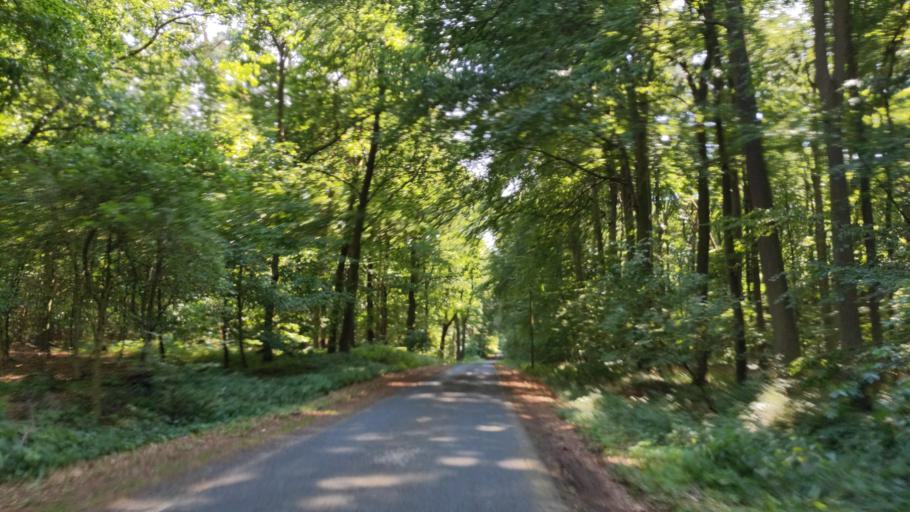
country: DE
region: Schleswig-Holstein
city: Buchholz
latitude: 53.7360
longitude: 10.7686
